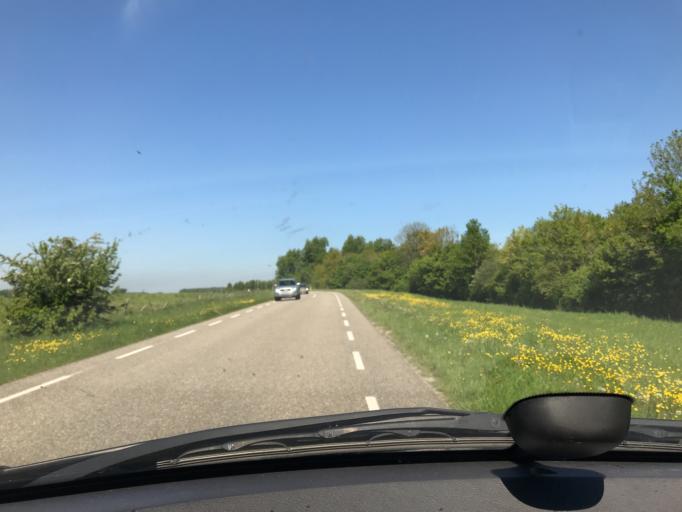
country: NL
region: Zeeland
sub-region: Gemeente Veere
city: Veere
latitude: 51.5094
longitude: 3.7018
